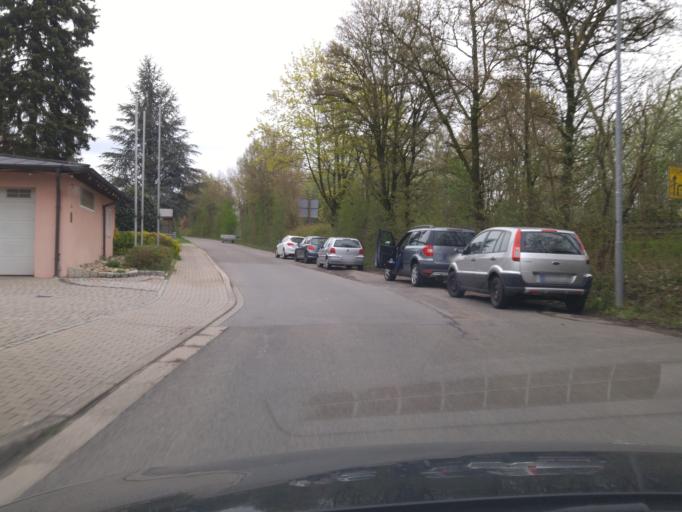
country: DE
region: Baden-Wuerttemberg
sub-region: Karlsruhe Region
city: Aglasterhausen
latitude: 49.3528
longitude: 8.9953
